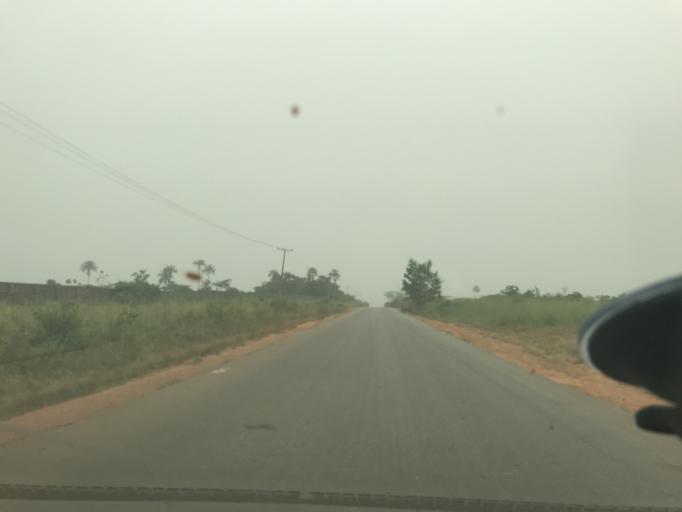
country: NG
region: Ogun
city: Owode
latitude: 6.8884
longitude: 3.5348
